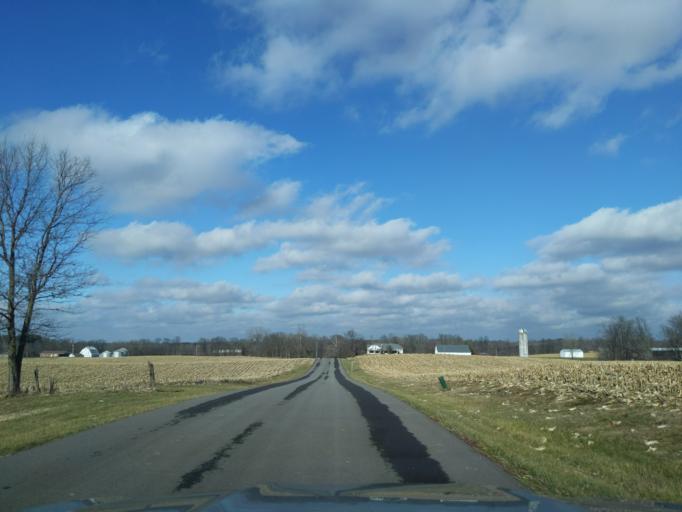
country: US
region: Indiana
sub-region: Decatur County
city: Greensburg
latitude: 39.2704
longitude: -85.4839
